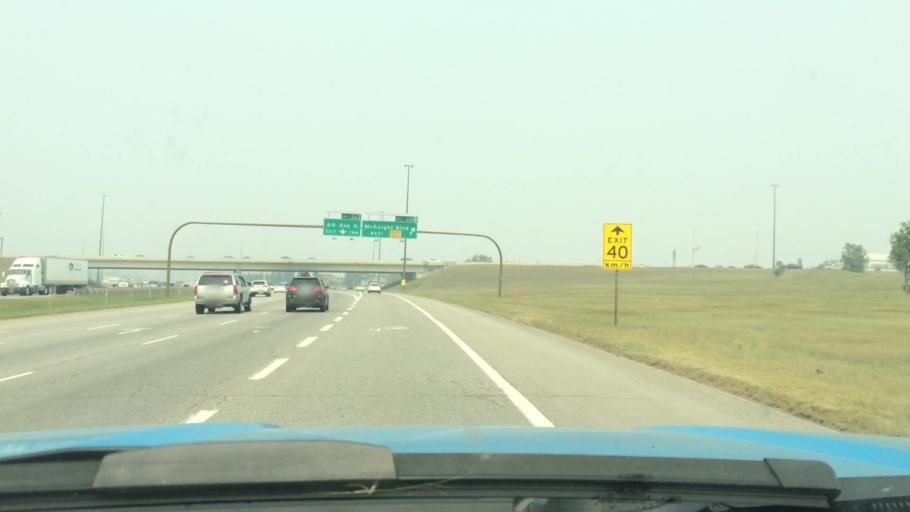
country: CA
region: Alberta
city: Calgary
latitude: 51.0939
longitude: -114.0396
